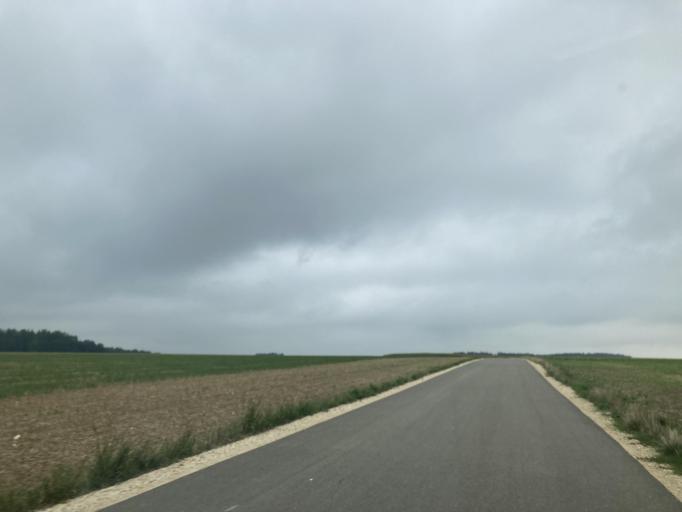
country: DE
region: Bavaria
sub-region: Swabia
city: Medlingen
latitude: 48.5772
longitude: 10.3081
